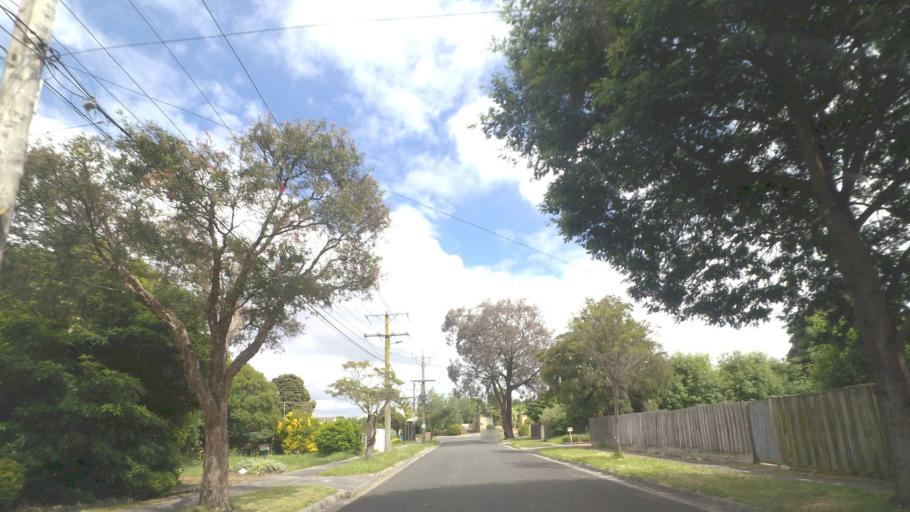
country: AU
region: Victoria
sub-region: Knox
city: Bayswater
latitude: -37.8470
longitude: 145.2651
